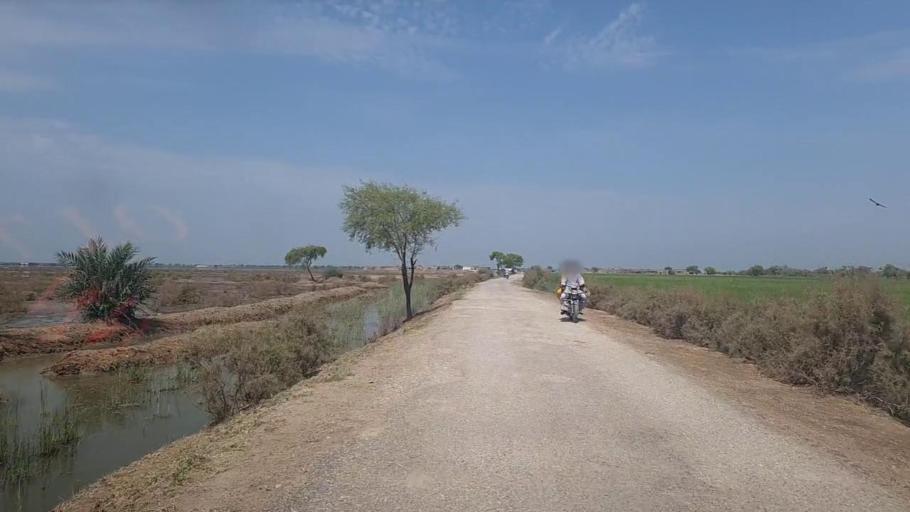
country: PK
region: Sindh
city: Thul
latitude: 28.2872
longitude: 68.6848
